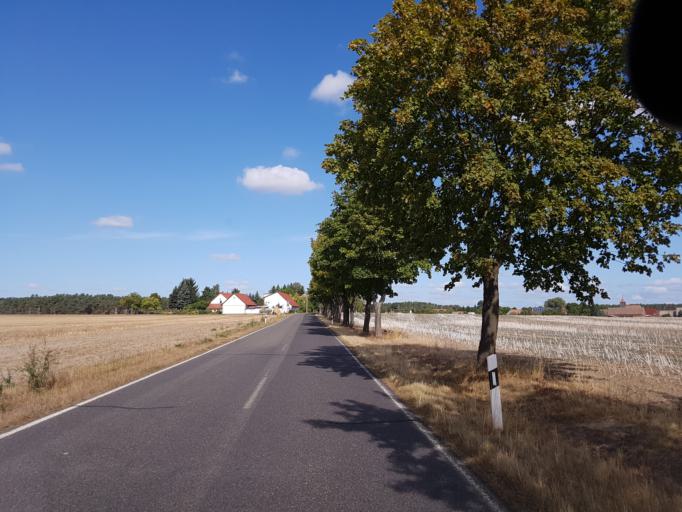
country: DE
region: Brandenburg
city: Sonnewalde
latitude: 51.7504
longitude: 13.6158
